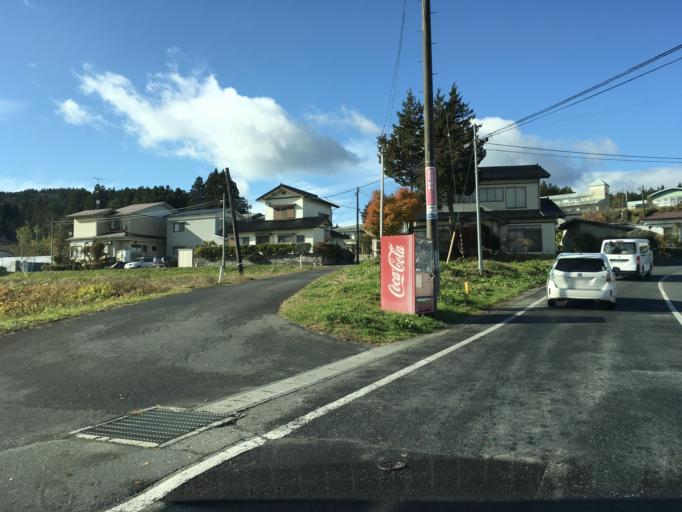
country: JP
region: Iwate
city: Ofunato
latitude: 38.9358
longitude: 141.4438
